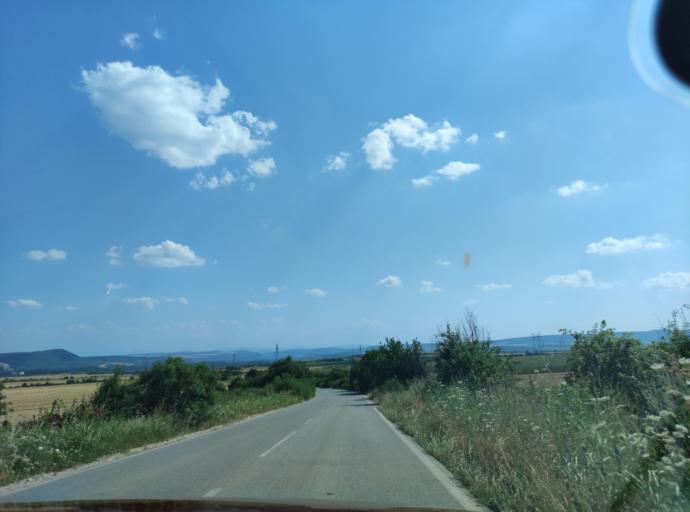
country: BG
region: Pleven
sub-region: Obshtina Cherven Bryag
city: Koynare
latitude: 43.3544
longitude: 24.0643
